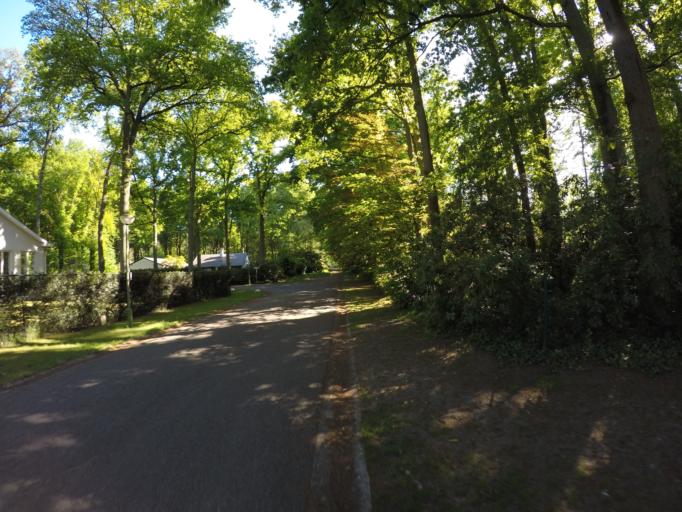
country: BE
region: Flanders
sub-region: Provincie Antwerpen
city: Schilde
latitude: 51.2533
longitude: 4.5518
